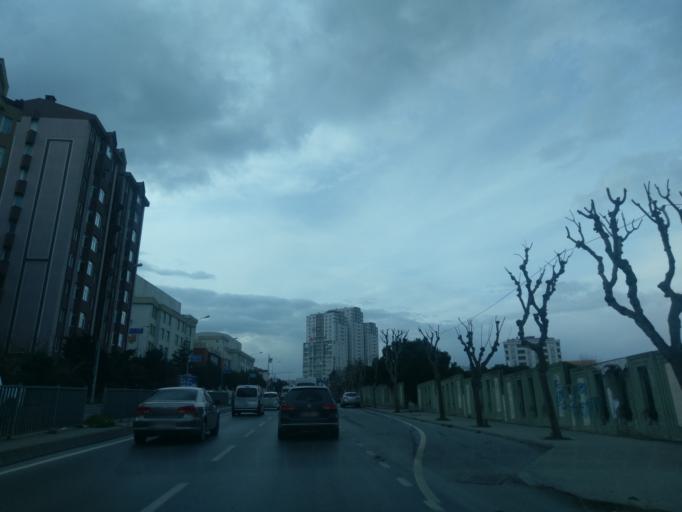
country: TR
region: Istanbul
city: Esenyurt
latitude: 41.0639
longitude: 28.6751
